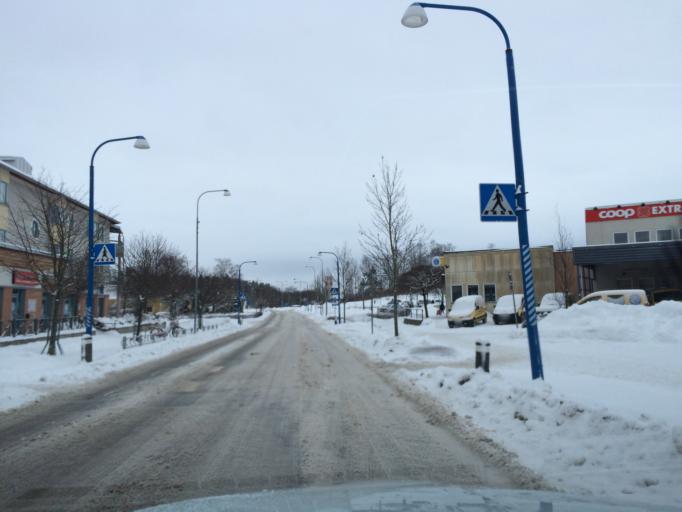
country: SE
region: Vaestmanland
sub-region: Hallstahammars Kommun
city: Hallstahammar
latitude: 59.6138
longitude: 16.2316
